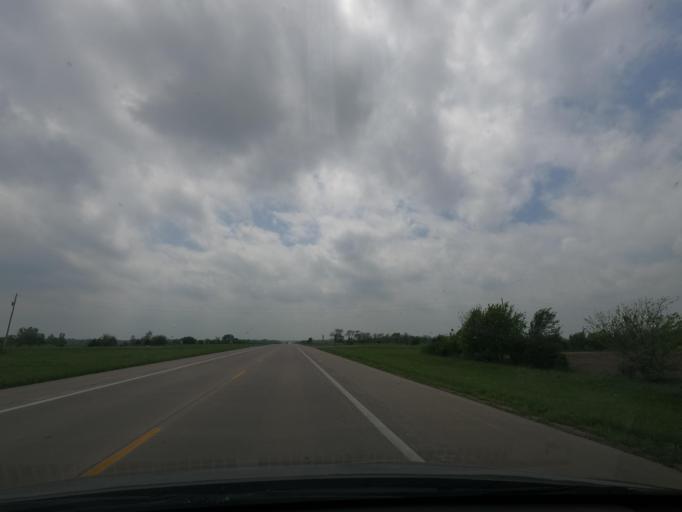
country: US
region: Kansas
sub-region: Labette County
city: Parsons
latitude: 37.3632
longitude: -95.3022
